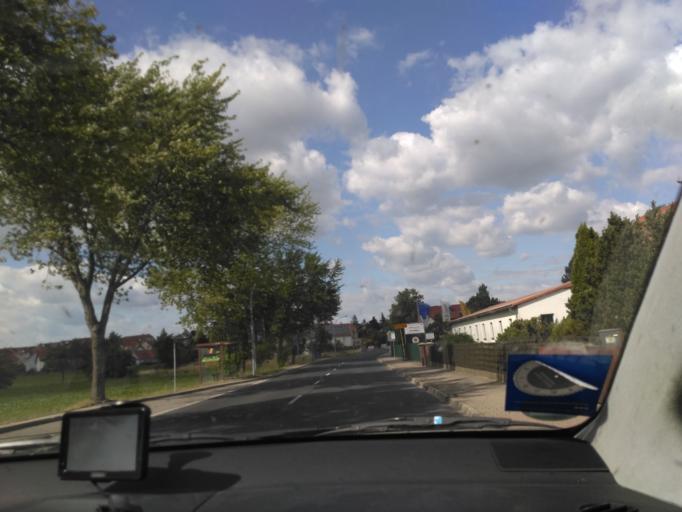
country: DE
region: Saxony
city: Meissen
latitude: 51.1923
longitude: 13.5038
